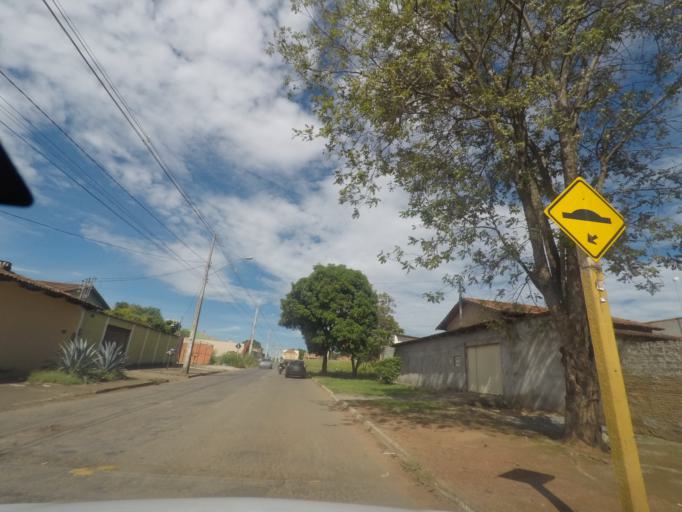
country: BR
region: Goias
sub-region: Aparecida De Goiania
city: Aparecida de Goiania
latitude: -16.8125
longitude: -49.2844
